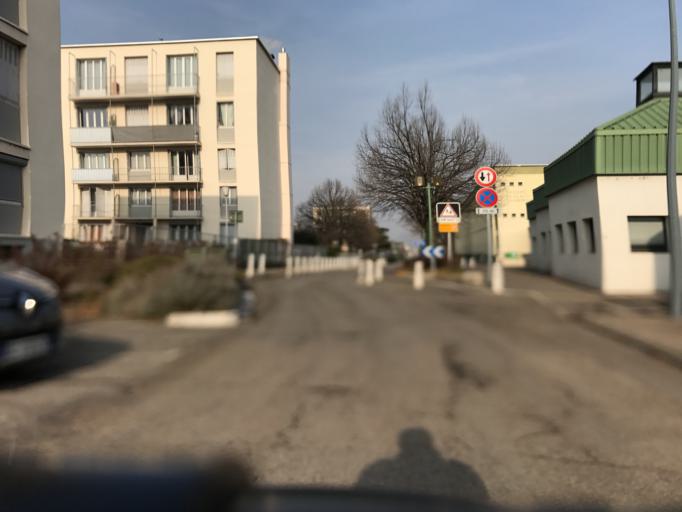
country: FR
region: Rhone-Alpes
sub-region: Departement de l'Isere
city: Seyssinet-Pariset
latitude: 45.1751
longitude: 5.6977
